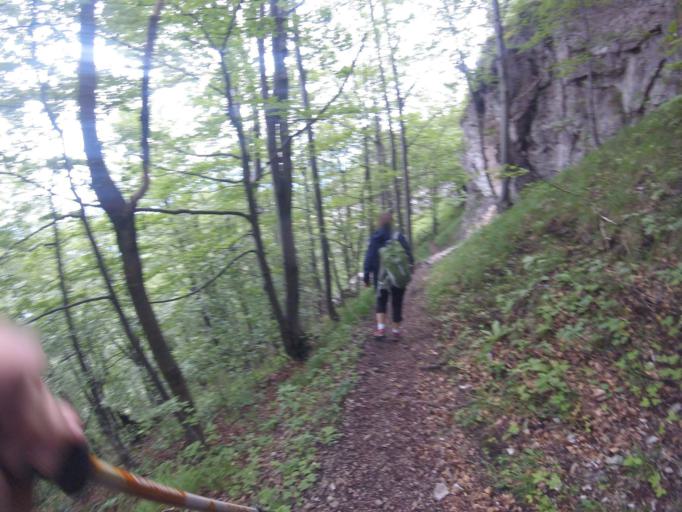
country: SK
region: Zilinsky
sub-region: Okres Zilina
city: Terchova
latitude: 49.2350
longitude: 19.0091
